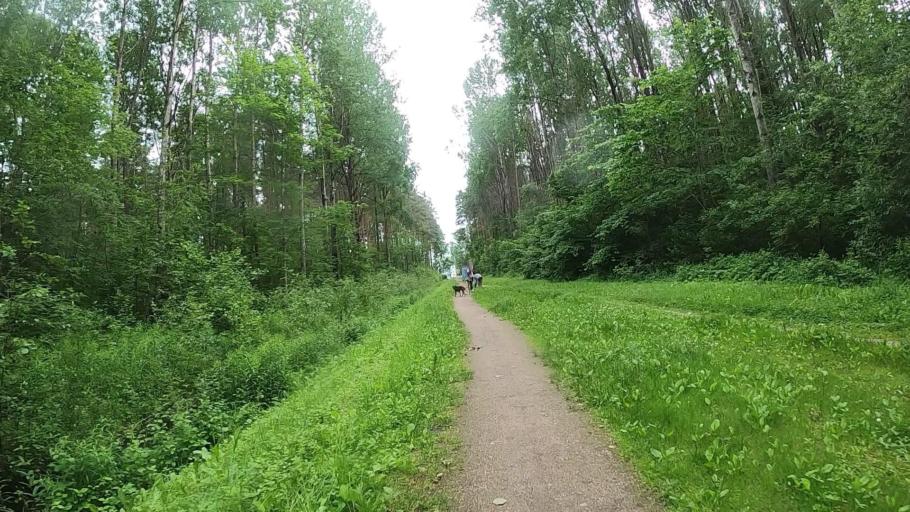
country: LV
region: Ozolnieku
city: Ozolnieki
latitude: 56.6736
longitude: 23.7537
